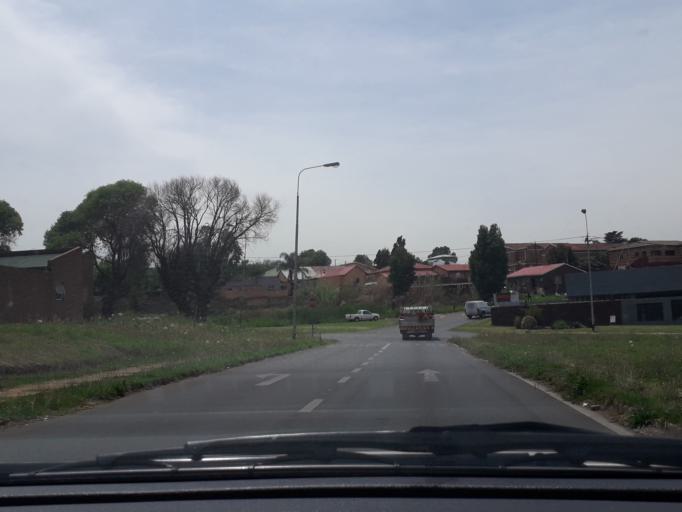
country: ZA
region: Gauteng
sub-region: City of Johannesburg Metropolitan Municipality
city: Roodepoort
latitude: -26.1796
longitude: 27.9347
